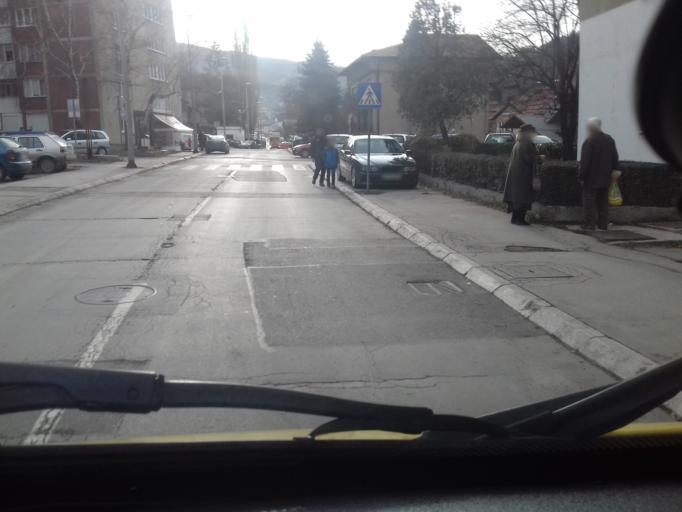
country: BA
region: Federation of Bosnia and Herzegovina
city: Zenica
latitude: 44.1934
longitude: 17.9100
